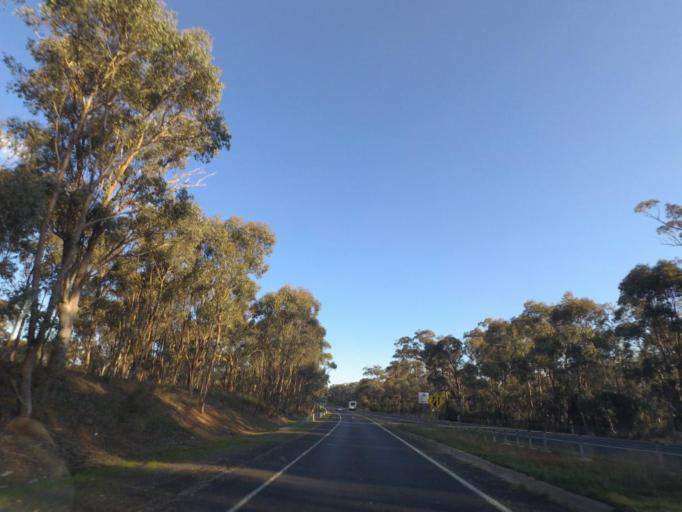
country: AU
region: Victoria
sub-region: Murrindindi
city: Kinglake West
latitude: -37.0672
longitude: 145.1018
